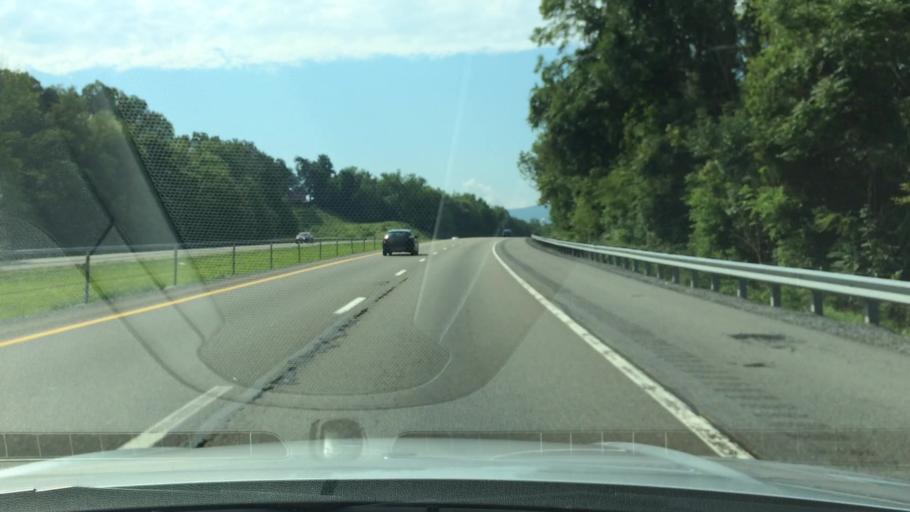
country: US
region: Tennessee
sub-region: Cocke County
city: Newport
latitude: 35.9577
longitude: -83.2089
